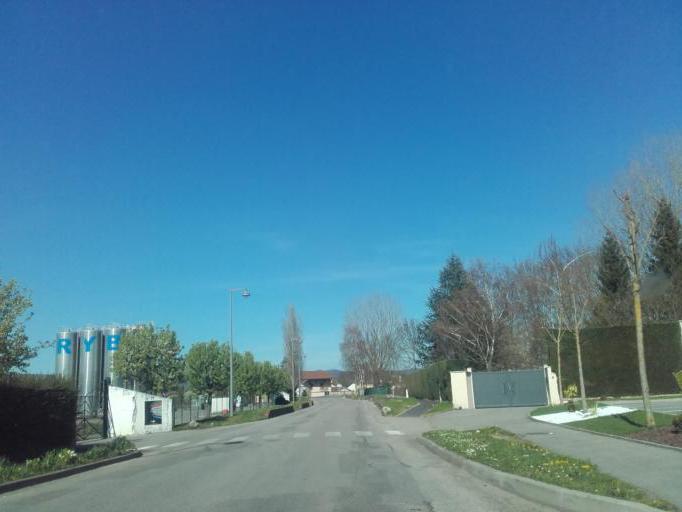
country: FR
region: Rhone-Alpes
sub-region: Departement de l'Isere
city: Saint-Etienne-de-Saint-Geoirs
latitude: 45.3414
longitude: 5.3493
